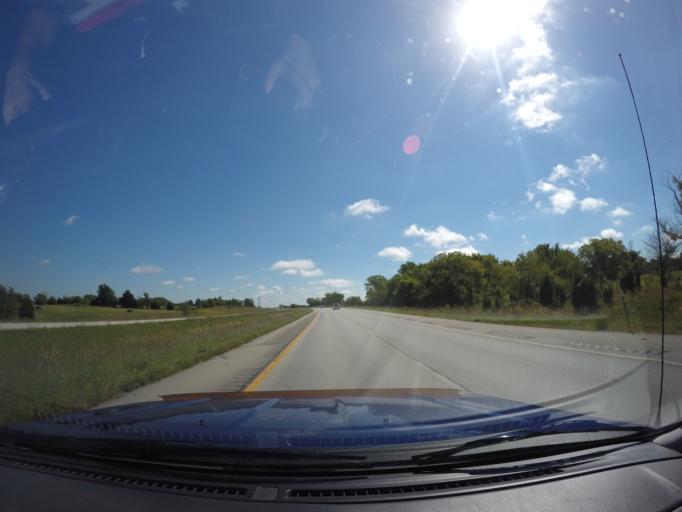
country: US
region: Kansas
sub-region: Douglas County
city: Eudora
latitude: 38.9293
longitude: -95.1062
